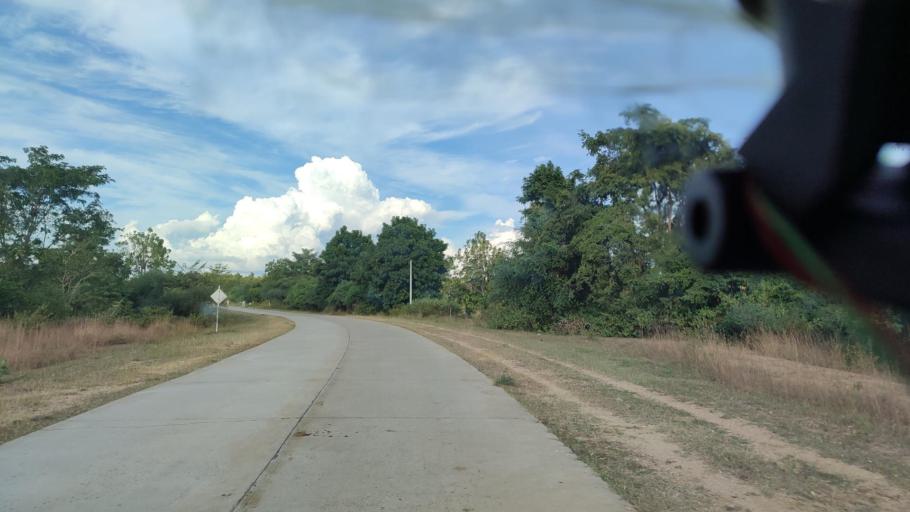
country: MM
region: Mandalay
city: Yamethin
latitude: 20.1012
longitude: 96.0365
